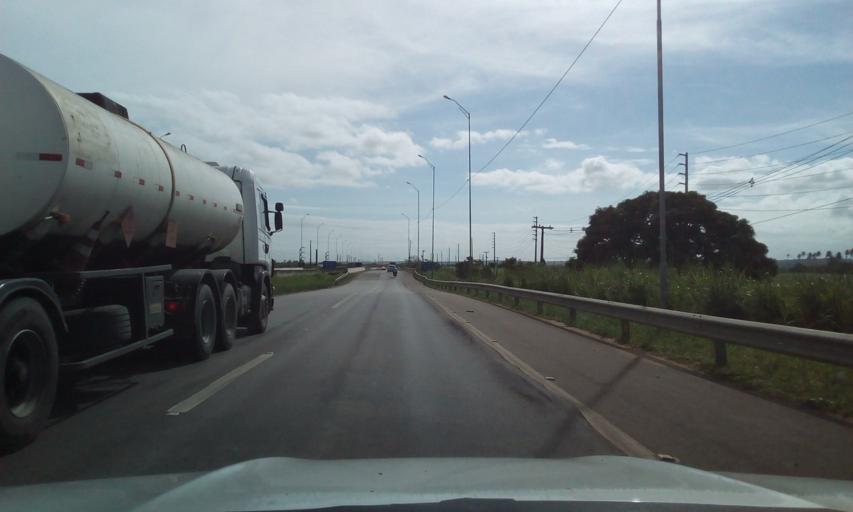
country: BR
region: Paraiba
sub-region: Bayeux
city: Bayeux
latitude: -7.1162
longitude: -34.9518
